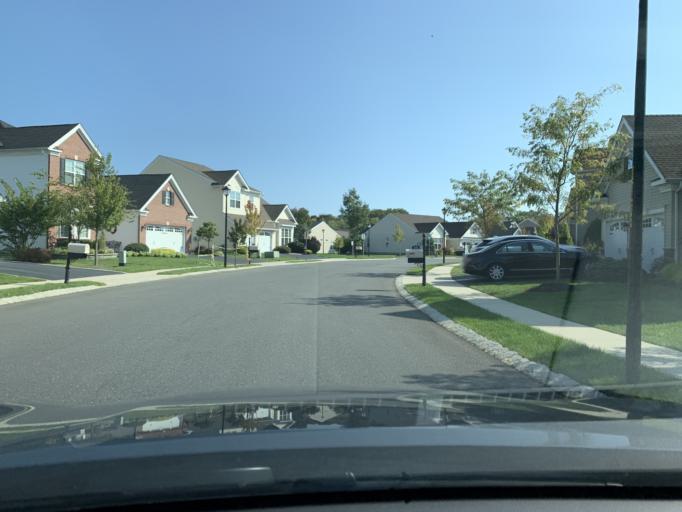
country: US
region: New Jersey
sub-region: Monmouth County
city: Shrewsbury
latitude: 40.3150
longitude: -74.0572
